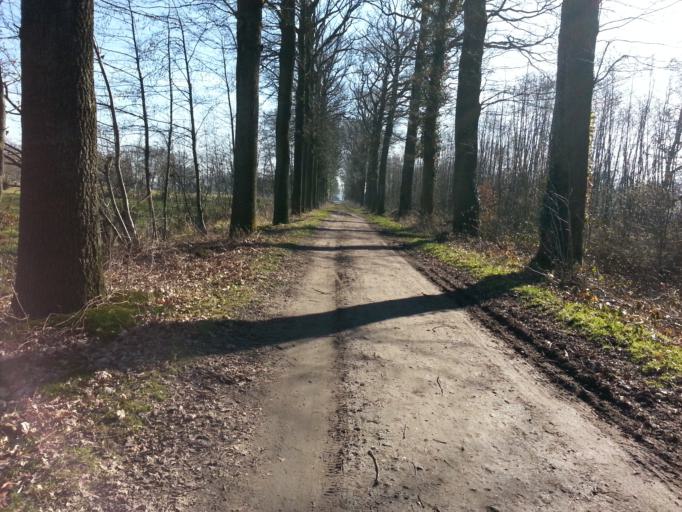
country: NL
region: Utrecht
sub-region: Gemeente Woudenberg
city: Woudenberg
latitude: 52.0880
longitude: 5.4210
